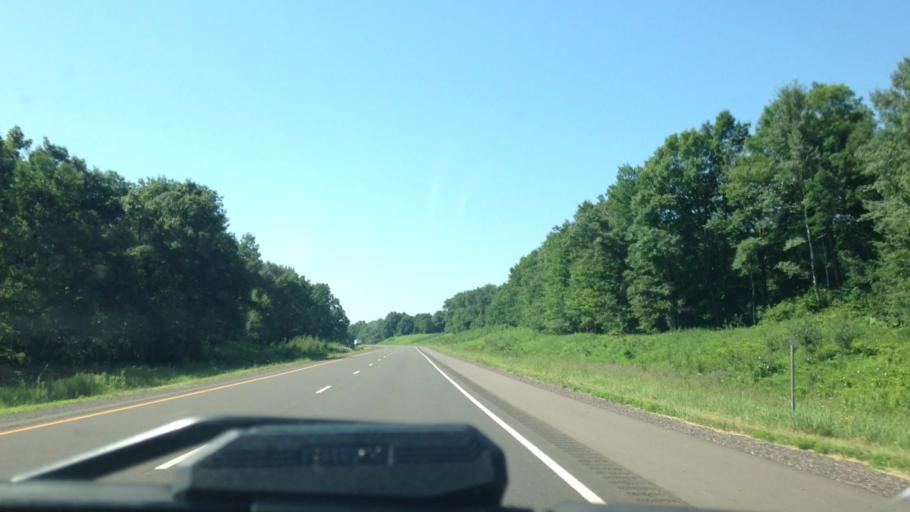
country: US
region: Wisconsin
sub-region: Washburn County
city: Spooner
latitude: 45.9491
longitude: -91.8286
